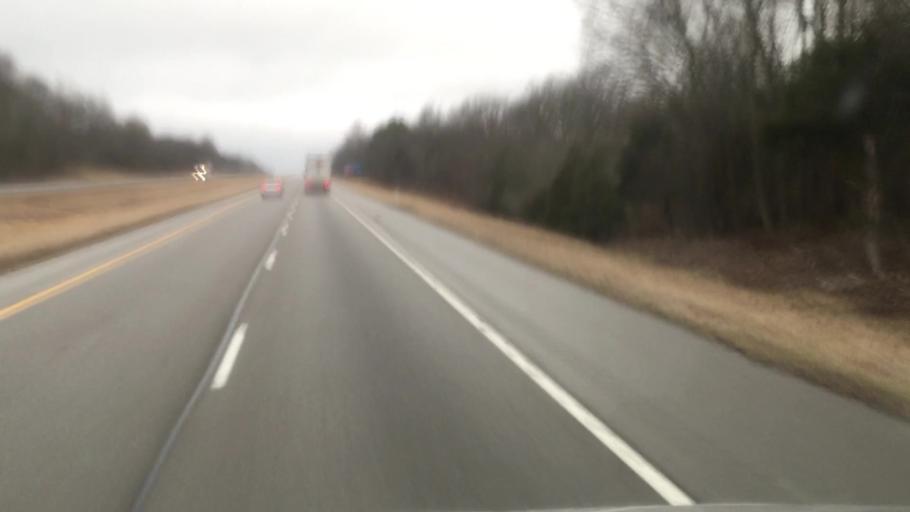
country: US
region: Illinois
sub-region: Johnson County
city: Vienna
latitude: 37.3951
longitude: -88.8440
